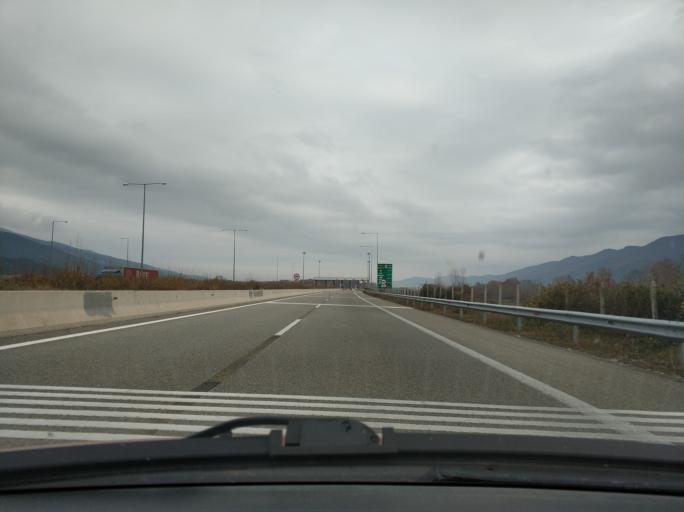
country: GR
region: East Macedonia and Thrace
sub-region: Nomos Kavalas
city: Palaiochori
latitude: 40.8566
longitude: 24.1592
